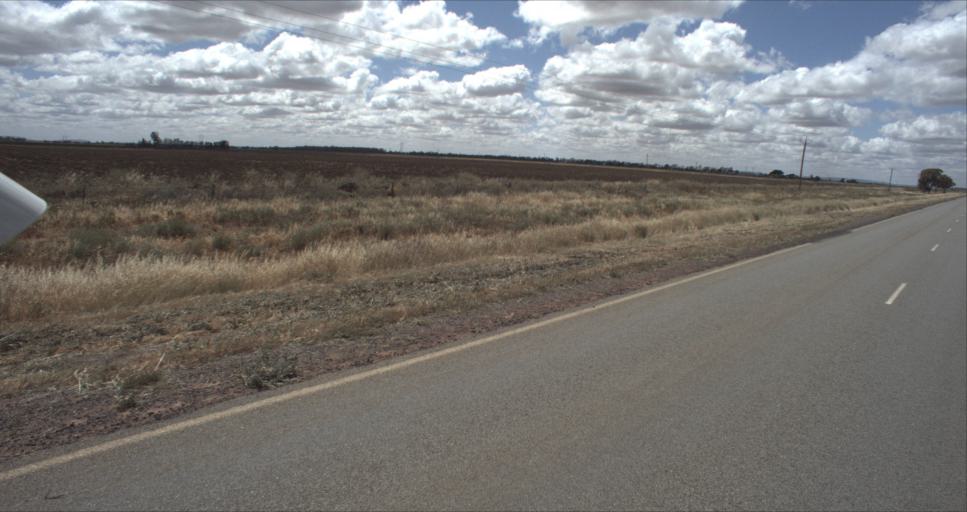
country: AU
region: New South Wales
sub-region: Murrumbidgee Shire
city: Darlington Point
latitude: -34.4954
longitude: 146.1755
